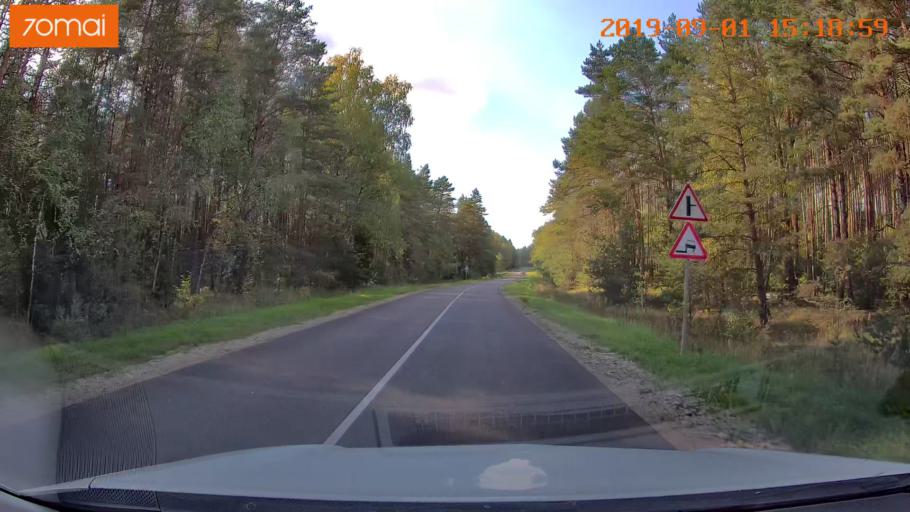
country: RU
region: Kaluga
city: Maloyaroslavets
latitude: 54.9113
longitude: 36.5014
